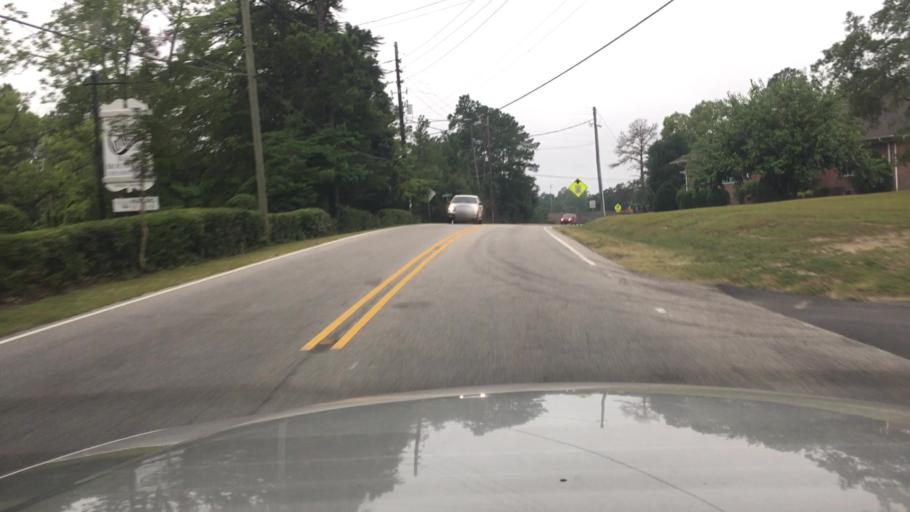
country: US
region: North Carolina
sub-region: Cumberland County
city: Hope Mills
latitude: 34.9742
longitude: -78.9521
